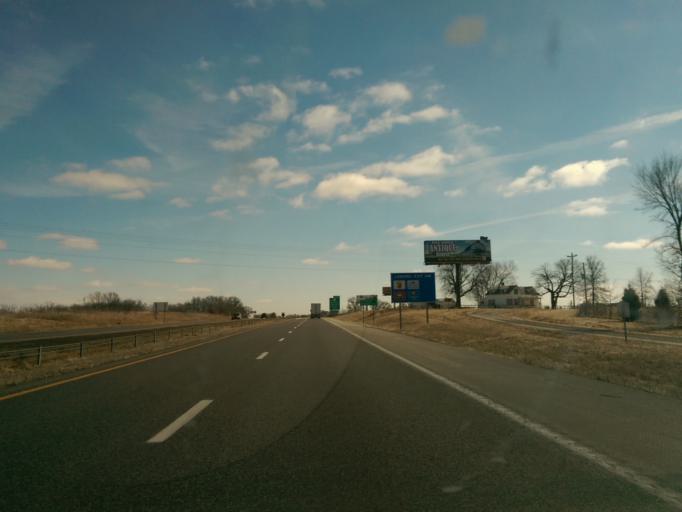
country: US
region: Missouri
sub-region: Callaway County
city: Fulton
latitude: 38.9498
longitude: -91.9620
